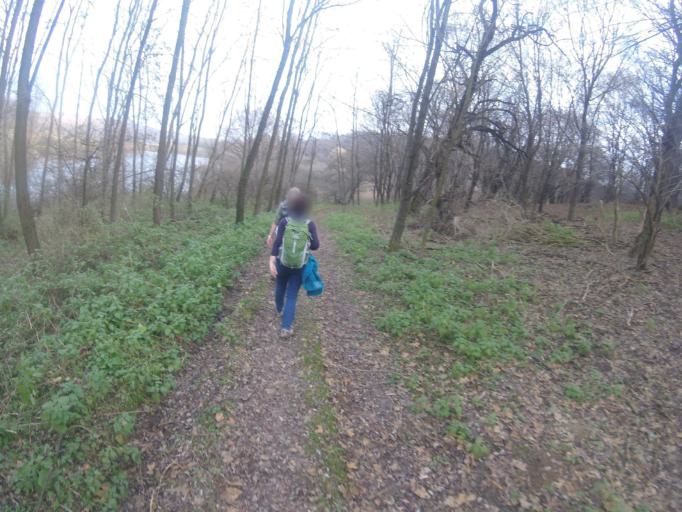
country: HU
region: Tolna
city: Bonyhad
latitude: 46.2684
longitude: 18.6284
